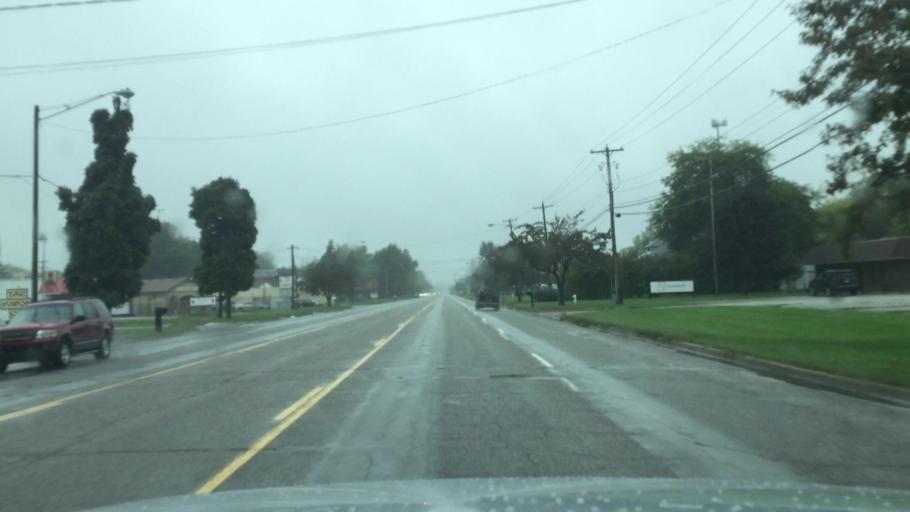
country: US
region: Michigan
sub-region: Saginaw County
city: Bridgeport
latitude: 43.3837
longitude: -83.8999
